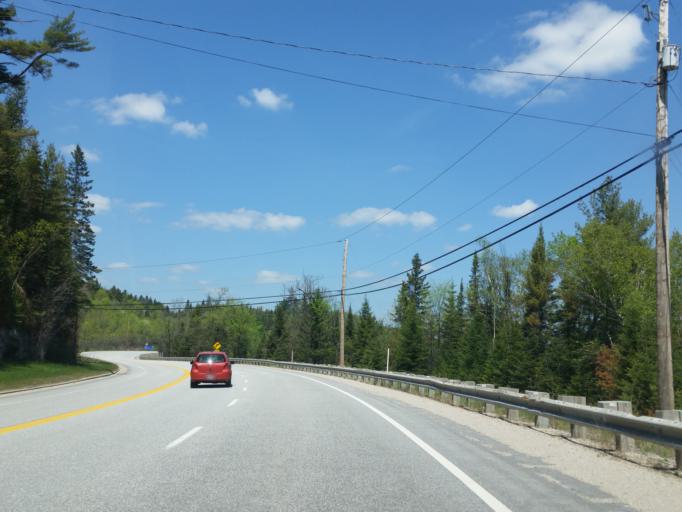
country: CA
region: Quebec
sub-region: Outaouais
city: Wakefield
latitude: 45.6625
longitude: -75.9260
